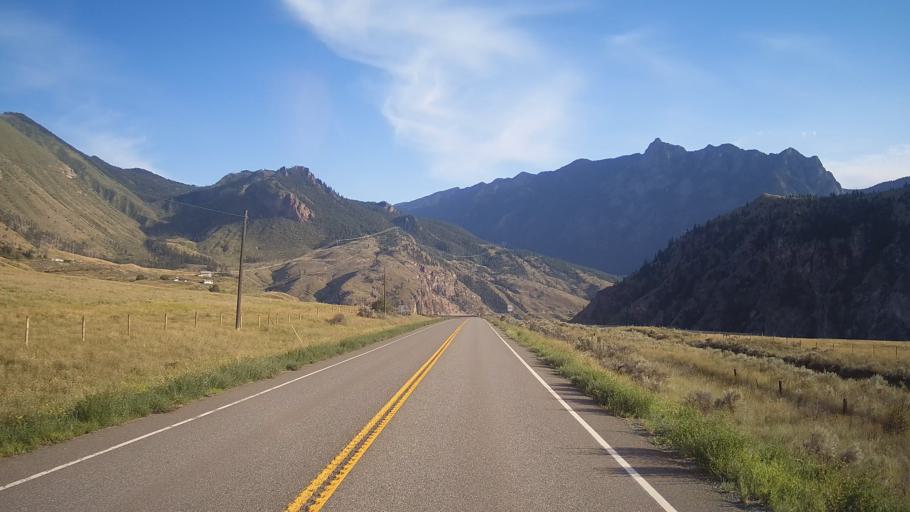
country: CA
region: British Columbia
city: Lillooet
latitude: 50.7730
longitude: -121.8383
